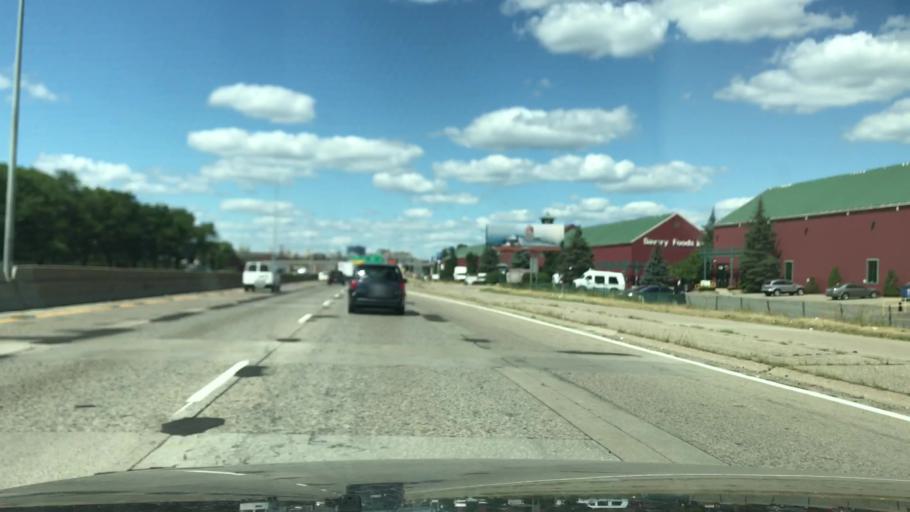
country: US
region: Michigan
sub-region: Kent County
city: Grand Rapids
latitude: 42.9445
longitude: -85.6764
